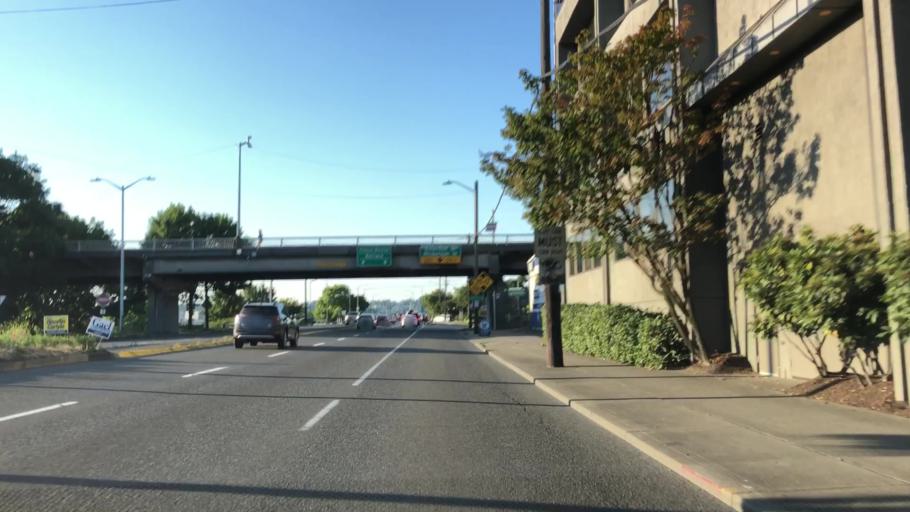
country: US
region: Washington
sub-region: King County
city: Seattle
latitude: 47.6524
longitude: -122.3761
